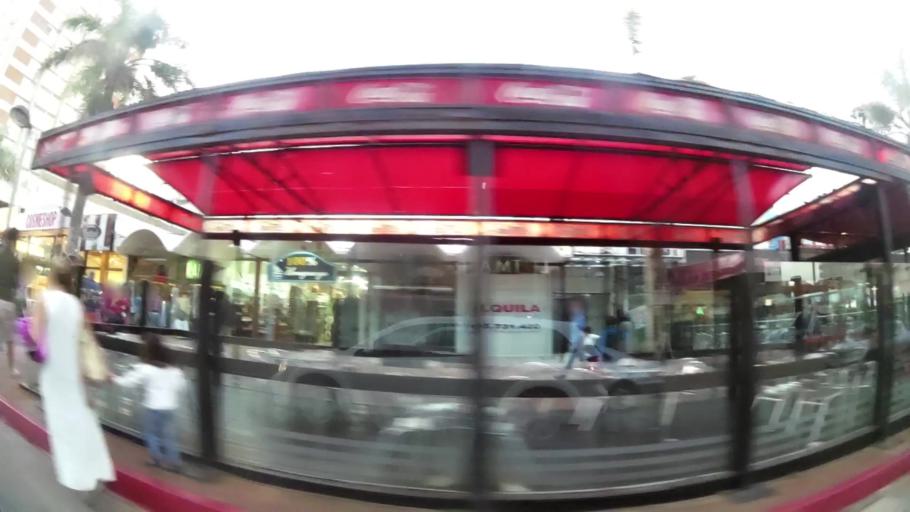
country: UY
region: Maldonado
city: Punta del Este
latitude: -34.9602
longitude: -54.9414
